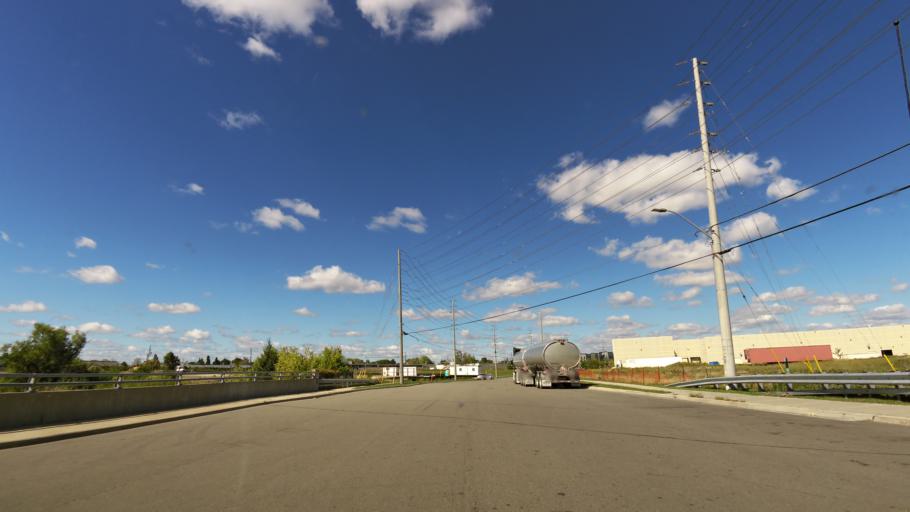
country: CA
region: Ontario
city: Etobicoke
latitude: 43.7072
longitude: -79.6541
